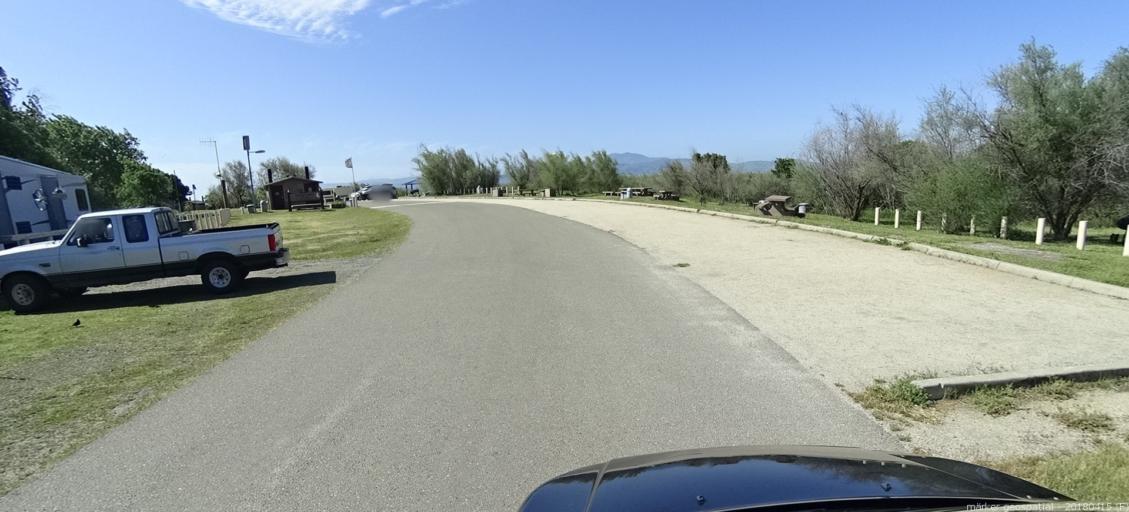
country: US
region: California
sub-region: Contra Costa County
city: Antioch
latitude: 38.0583
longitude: -121.7863
